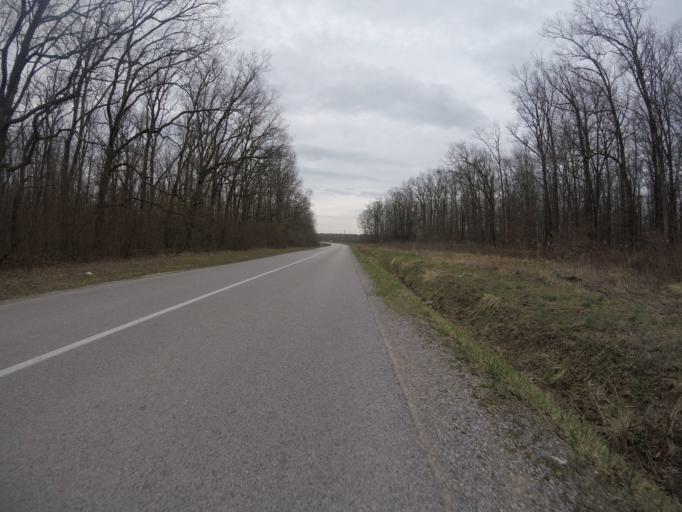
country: HR
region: Zagrebacka
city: Lukavec
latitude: 45.6902
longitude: 15.9814
